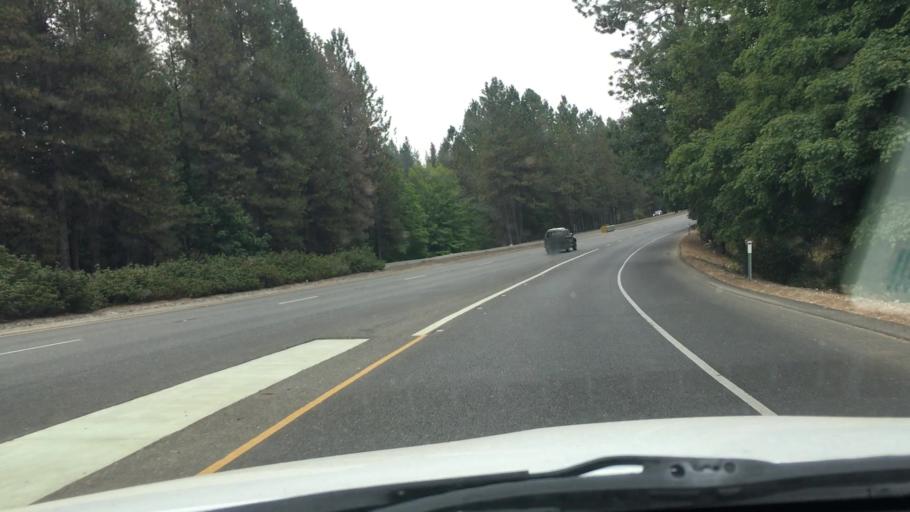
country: US
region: California
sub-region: Nevada County
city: Nevada City
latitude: 39.2576
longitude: -121.0187
